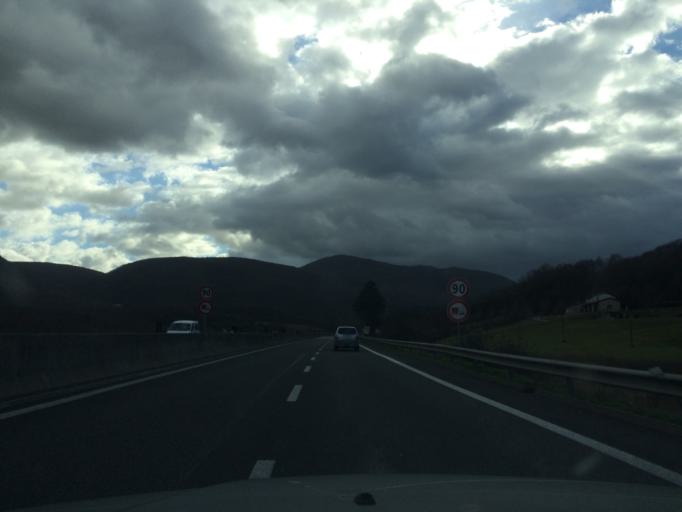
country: IT
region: Umbria
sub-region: Provincia di Terni
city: Acquasparta
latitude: 42.7200
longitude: 12.5496
